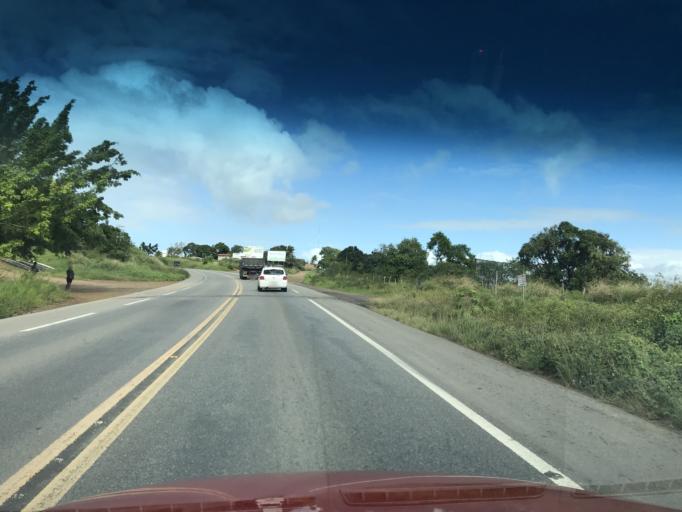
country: BR
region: Bahia
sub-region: Conceicao Do Almeida
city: Muritiba
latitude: -12.8947
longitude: -39.2334
